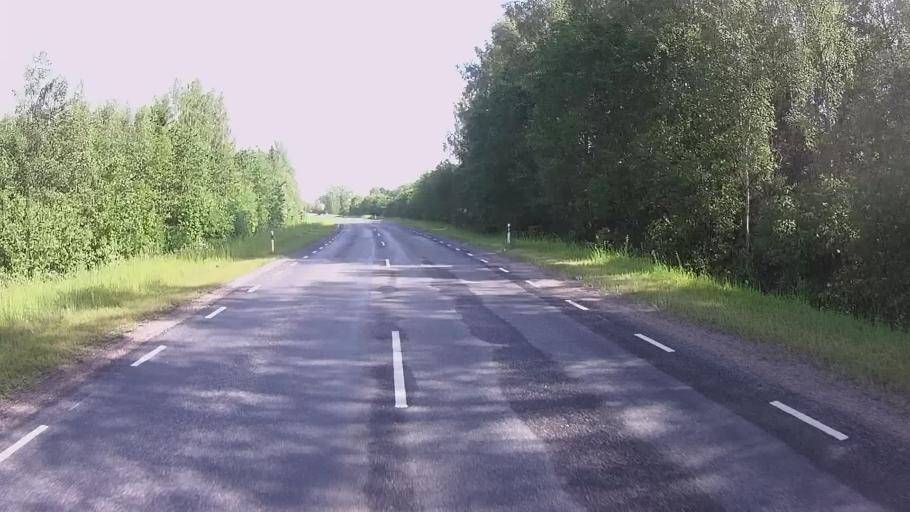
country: EE
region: Valgamaa
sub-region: Torva linn
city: Torva
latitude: 58.0776
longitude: 26.0419
